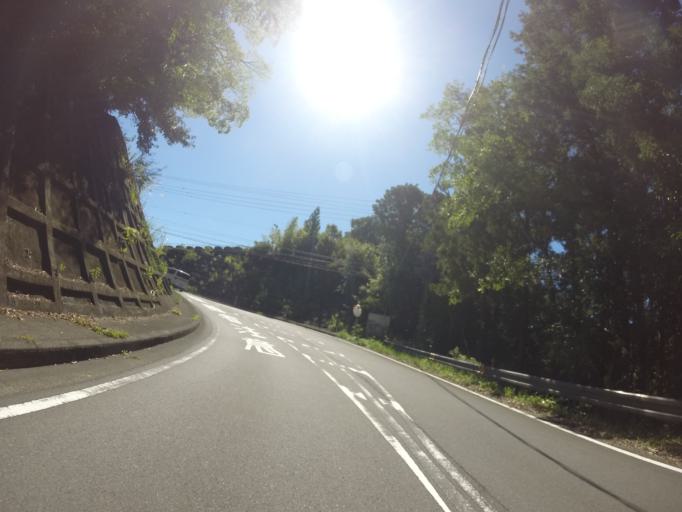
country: JP
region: Shizuoka
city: Kanaya
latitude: 34.9102
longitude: 138.1256
